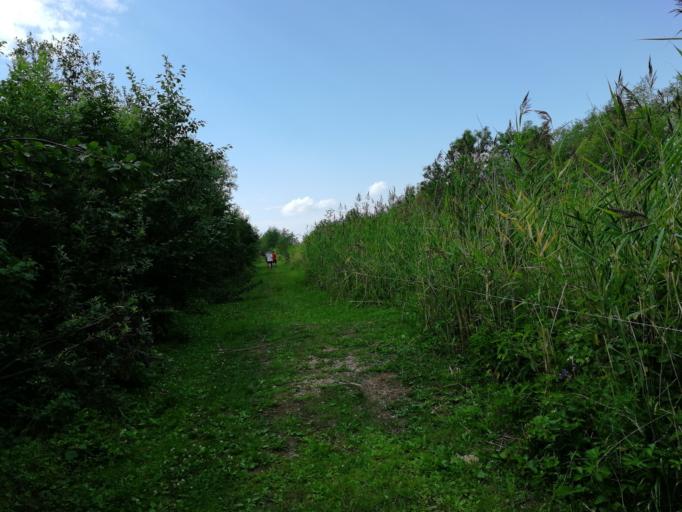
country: EE
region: Laeaene
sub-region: Lihula vald
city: Lihula
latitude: 58.7261
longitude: 23.8066
